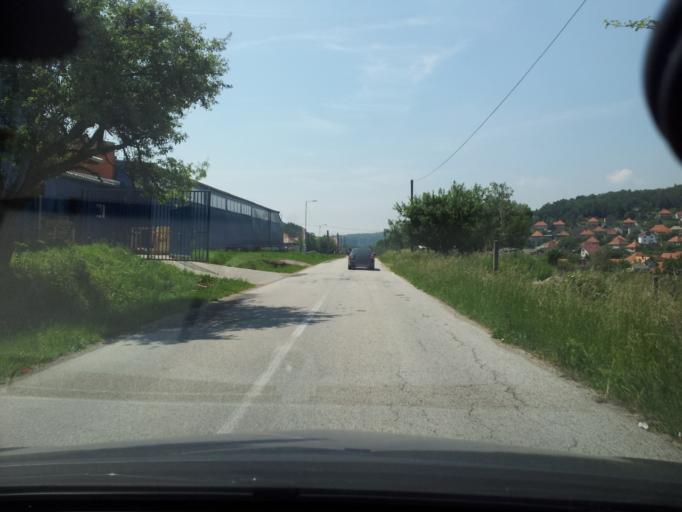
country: SK
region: Nitriansky
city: Zlate Moravce
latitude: 48.5018
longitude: 18.4289
